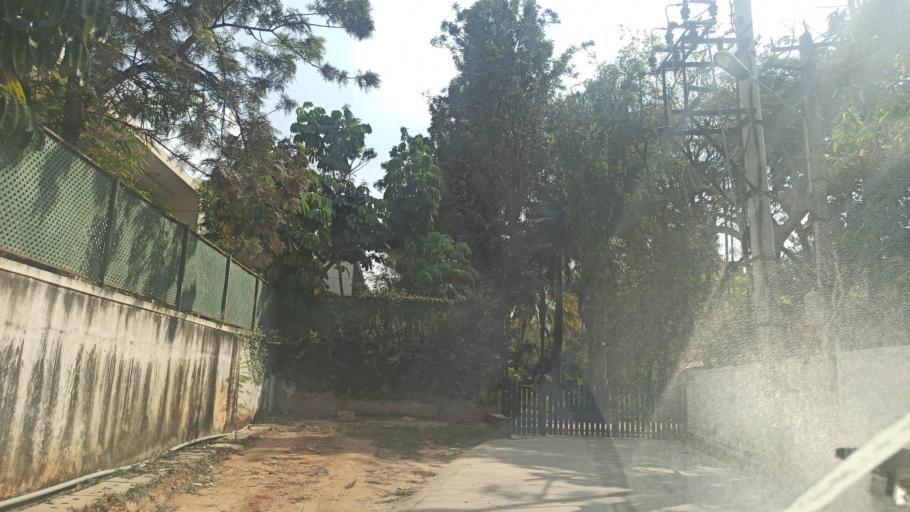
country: IN
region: Karnataka
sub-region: Bangalore Urban
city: Yelahanka
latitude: 13.1154
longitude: 77.6123
